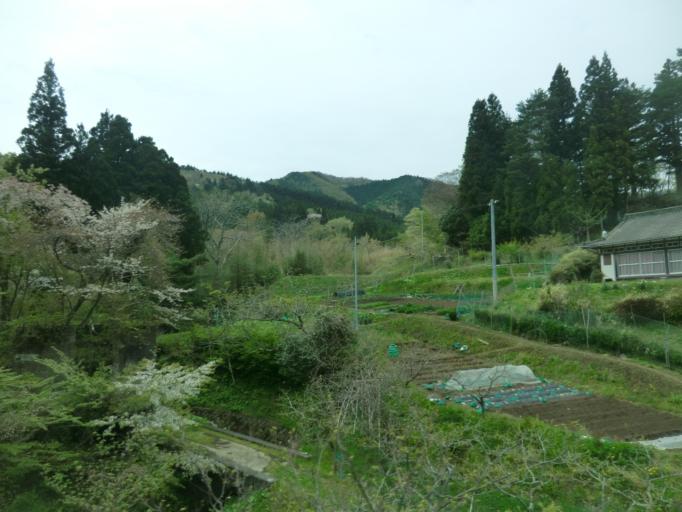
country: JP
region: Iwate
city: Ofunato
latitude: 39.0852
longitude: 141.8105
